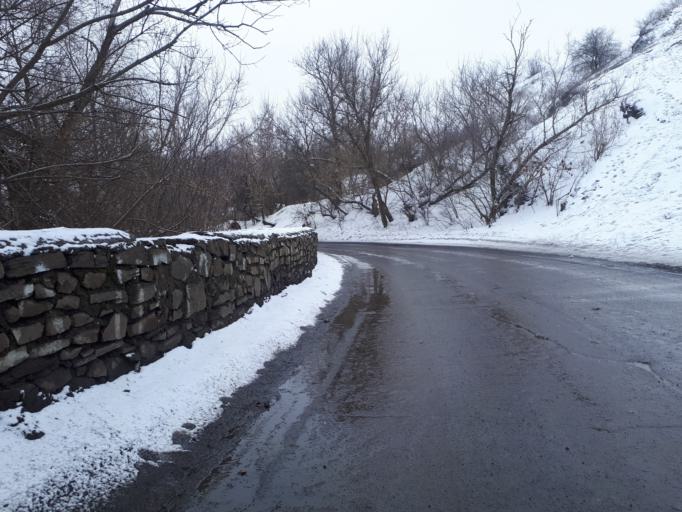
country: RU
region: Rostov
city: Krasnyy Sulin
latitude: 47.8999
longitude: 40.0480
